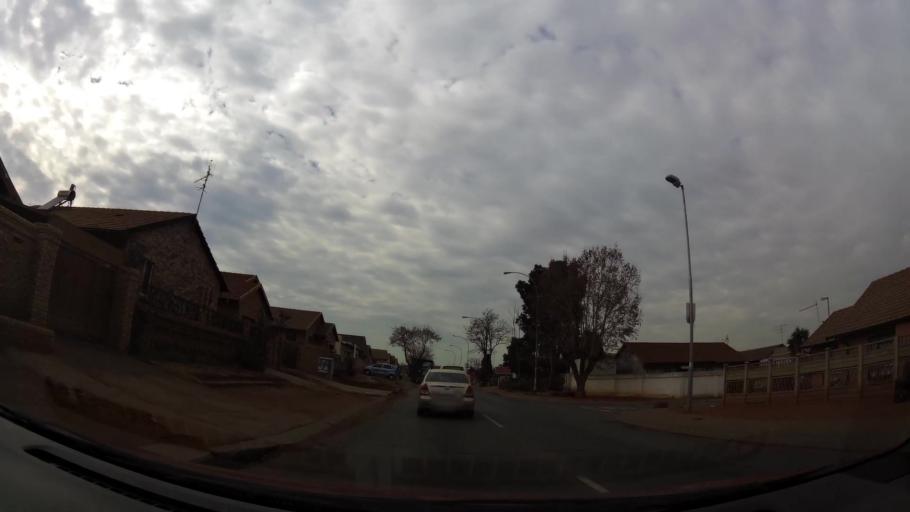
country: ZA
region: Gauteng
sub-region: City of Johannesburg Metropolitan Municipality
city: Soweto
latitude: -26.2690
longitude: 27.8301
